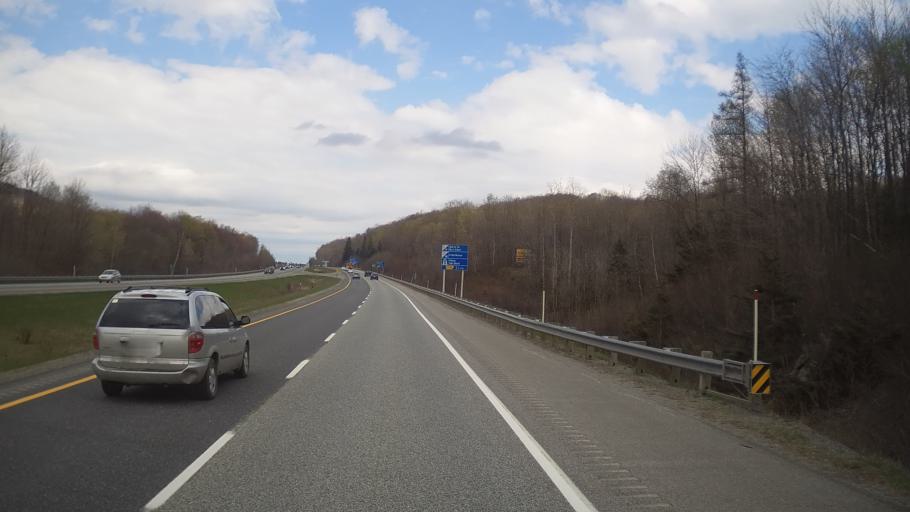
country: CA
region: Quebec
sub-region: Estrie
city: Magog
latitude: 45.2892
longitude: -72.2532
